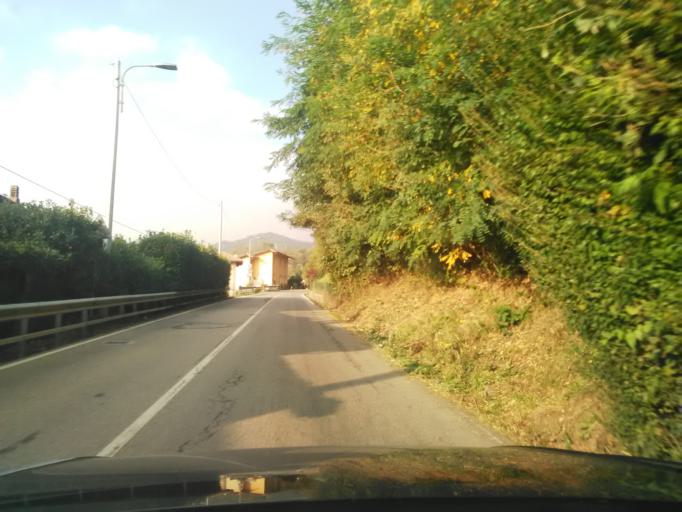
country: IT
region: Piedmont
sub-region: Provincia di Biella
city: Tollegno
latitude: 45.5834
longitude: 8.0601
